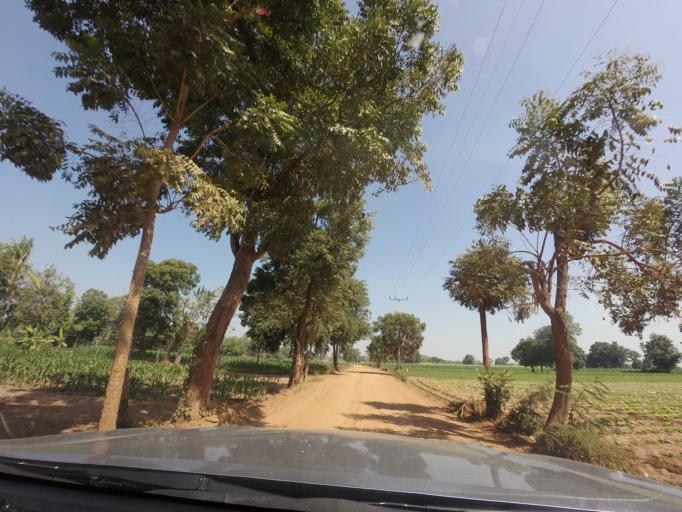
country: TH
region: Sukhothai
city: Sawankhalok
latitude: 17.2552
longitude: 99.7786
